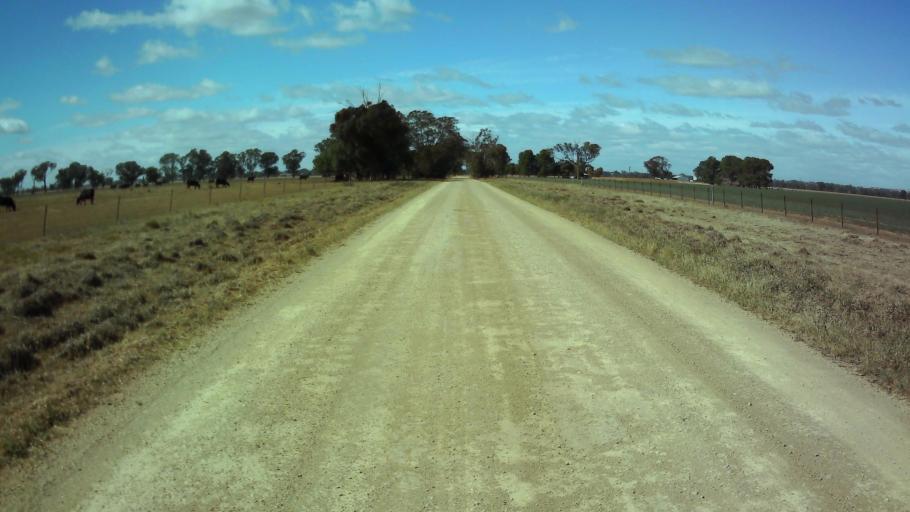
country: AU
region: New South Wales
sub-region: Weddin
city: Grenfell
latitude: -34.0254
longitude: 148.3183
